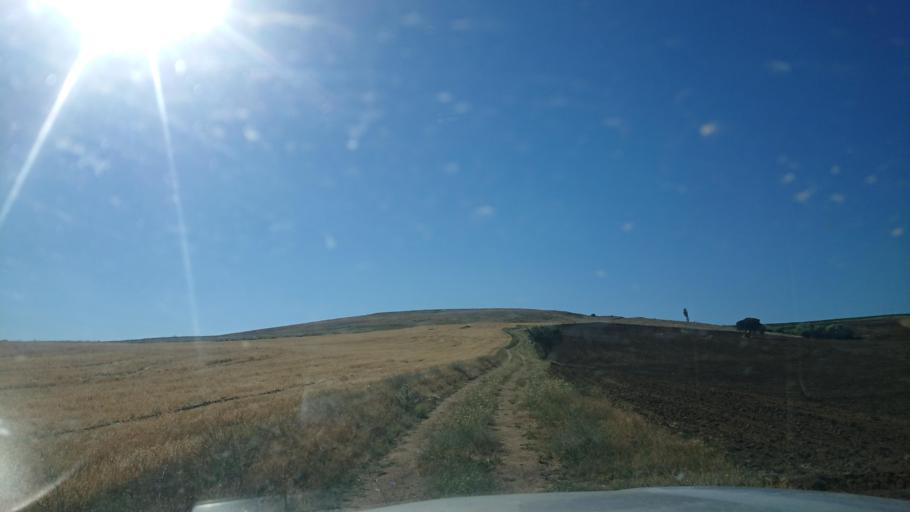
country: TR
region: Aksaray
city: Agacoren
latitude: 38.8397
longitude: 33.9337
